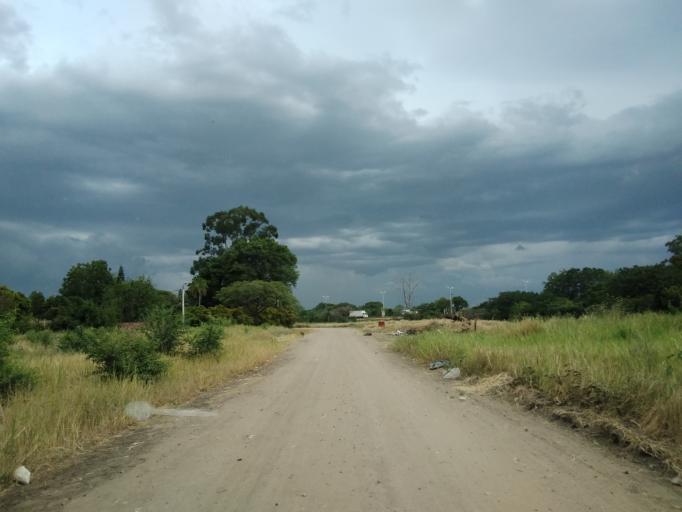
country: AR
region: Corrientes
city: Corrientes
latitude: -27.5227
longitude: -58.7965
